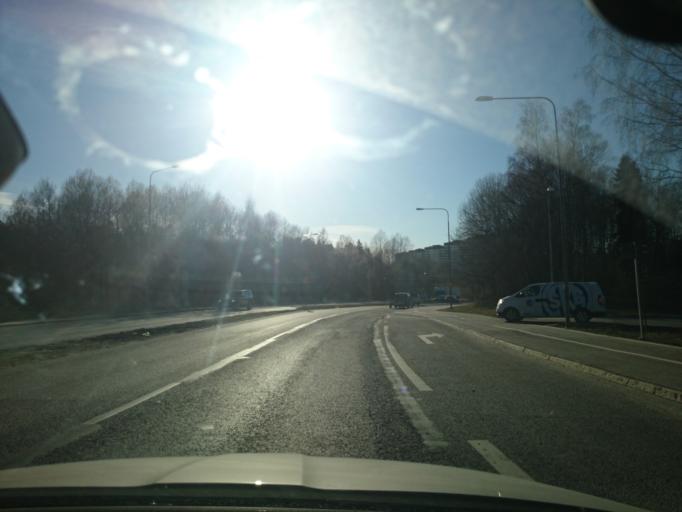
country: SE
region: Stockholm
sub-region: Stockholms Kommun
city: Arsta
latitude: 59.2597
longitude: 18.0405
